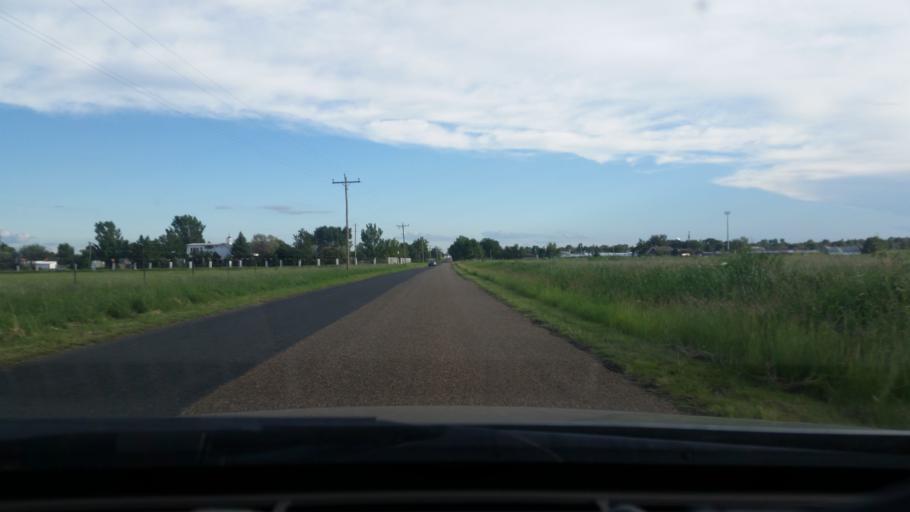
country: US
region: New Mexico
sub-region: Curry County
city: Clovis
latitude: 34.4554
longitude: -103.1784
